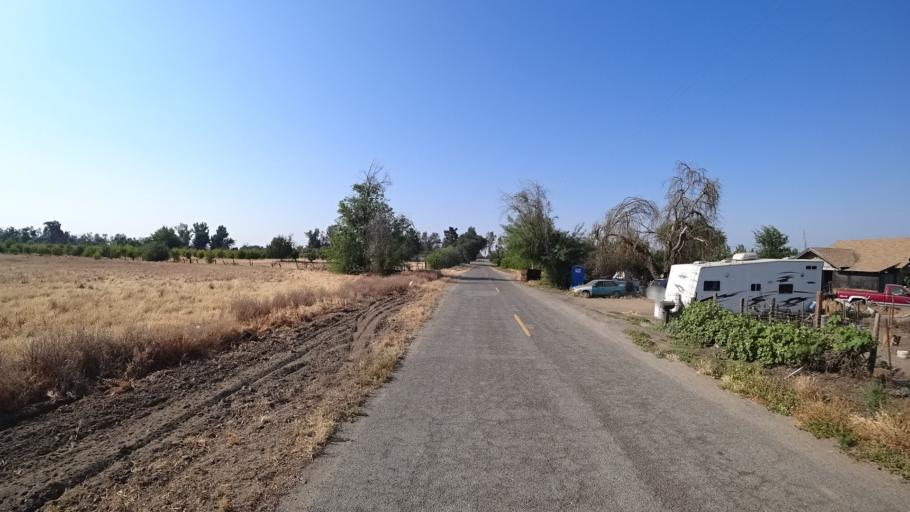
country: US
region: California
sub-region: Kings County
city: Lemoore
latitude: 36.3625
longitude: -119.8161
